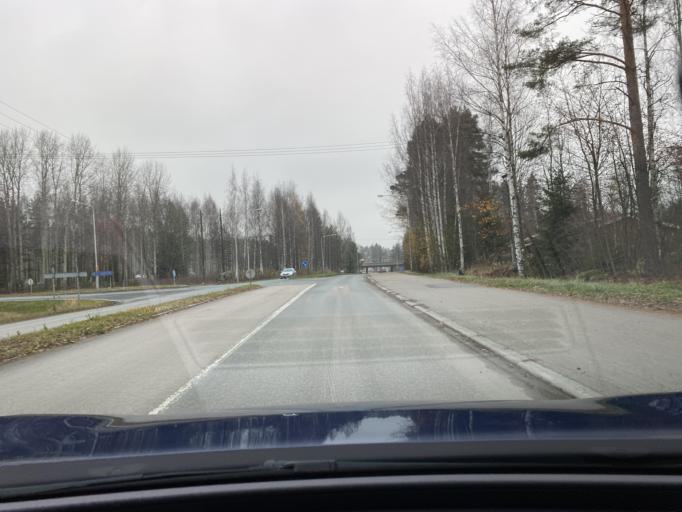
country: FI
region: Pirkanmaa
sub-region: Tampere
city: Nokia
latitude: 61.4615
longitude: 23.5040
